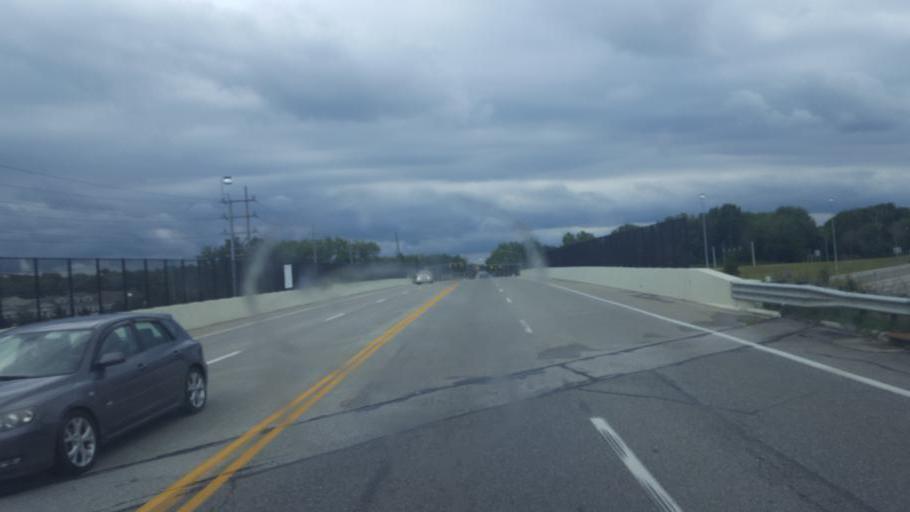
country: US
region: Ohio
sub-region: Lake County
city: Fairport Harbor
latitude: 41.7183
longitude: -81.2988
